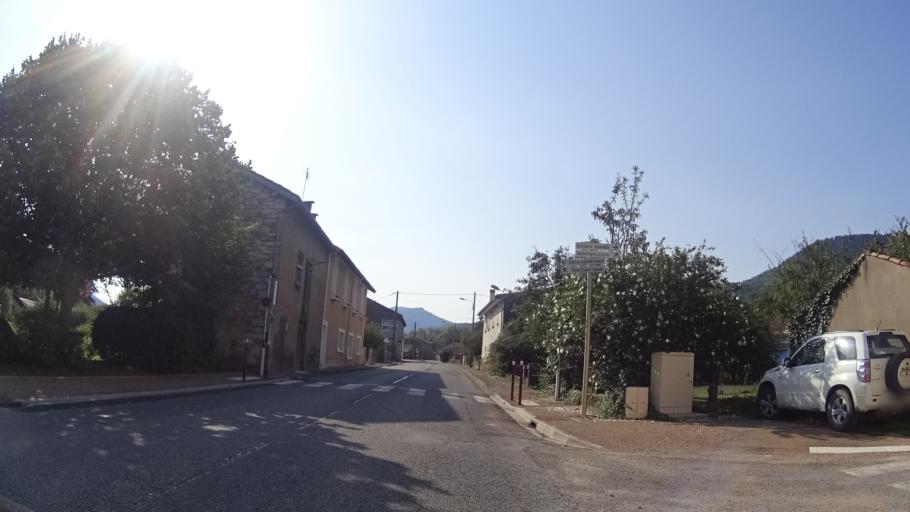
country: FR
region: Midi-Pyrenees
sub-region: Departement de l'Ariege
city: Belesta
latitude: 42.9165
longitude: 1.9029
